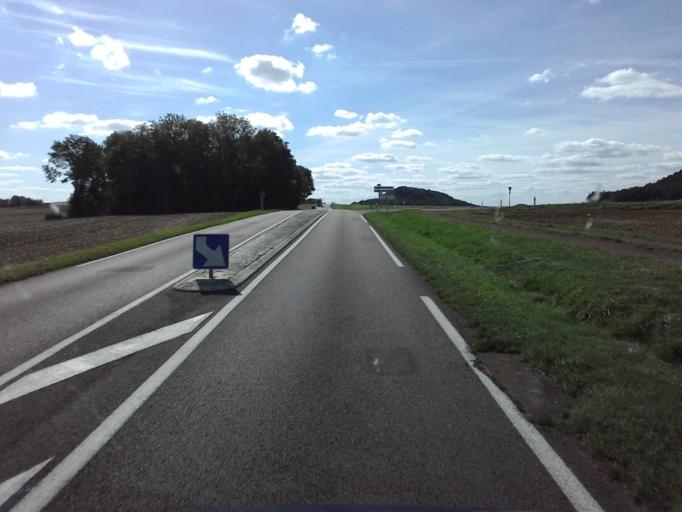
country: FR
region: Bourgogne
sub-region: Departement de la Cote-d'Or
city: Chatillon-sur-Seine
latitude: 47.9061
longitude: 4.6286
